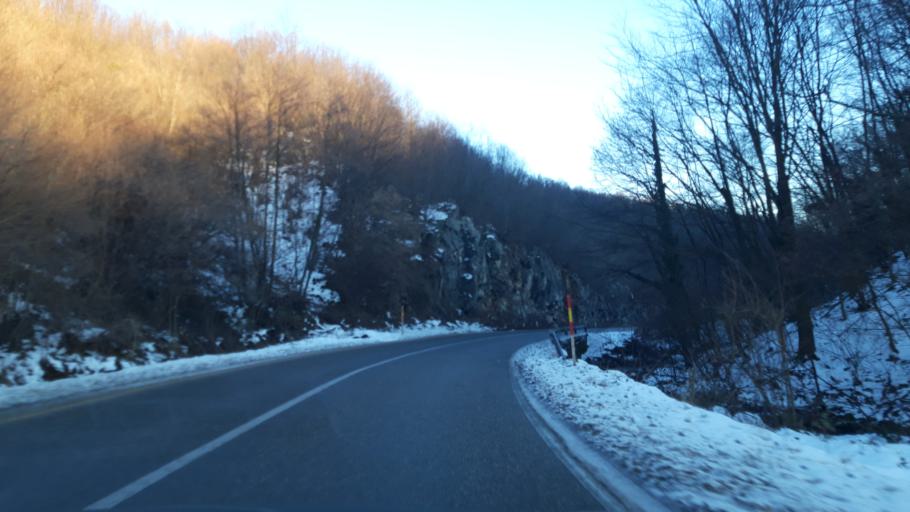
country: BA
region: Republika Srpska
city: Vlasenica
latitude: 44.1846
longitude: 18.9721
